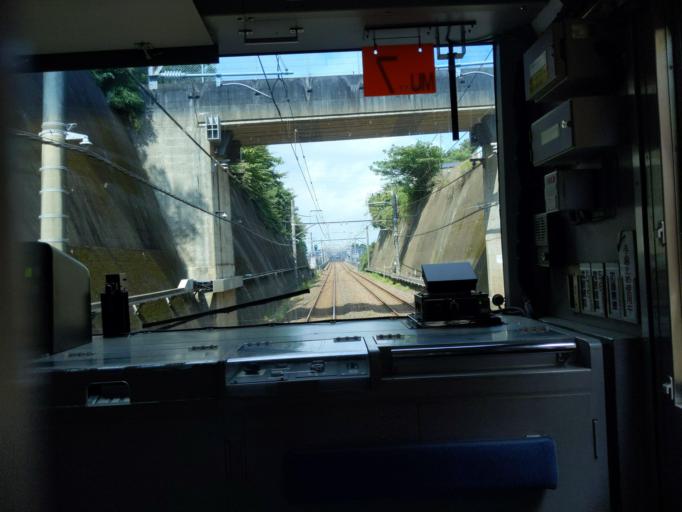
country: JP
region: Chiba
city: Matsudo
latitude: 35.8034
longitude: 139.9349
